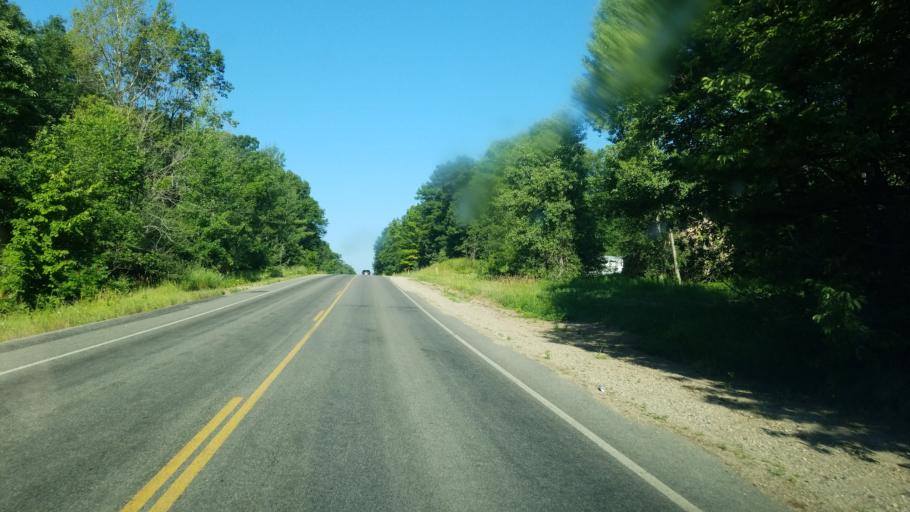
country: US
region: Michigan
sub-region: Montcalm County
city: Howard City
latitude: 43.4898
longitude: -85.4709
